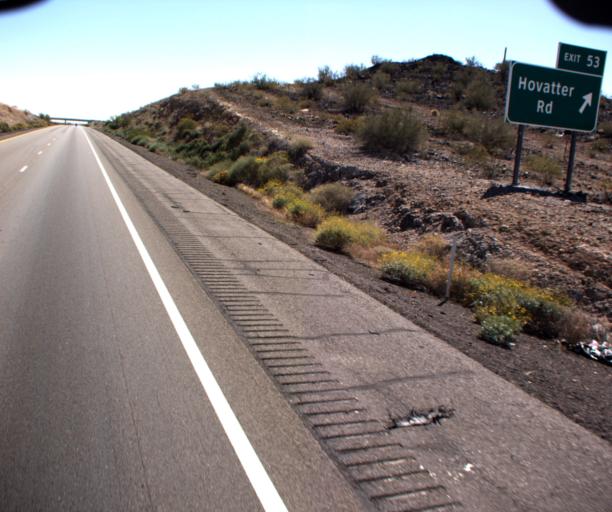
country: US
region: Arizona
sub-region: La Paz County
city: Salome
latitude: 33.6101
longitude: -113.6289
